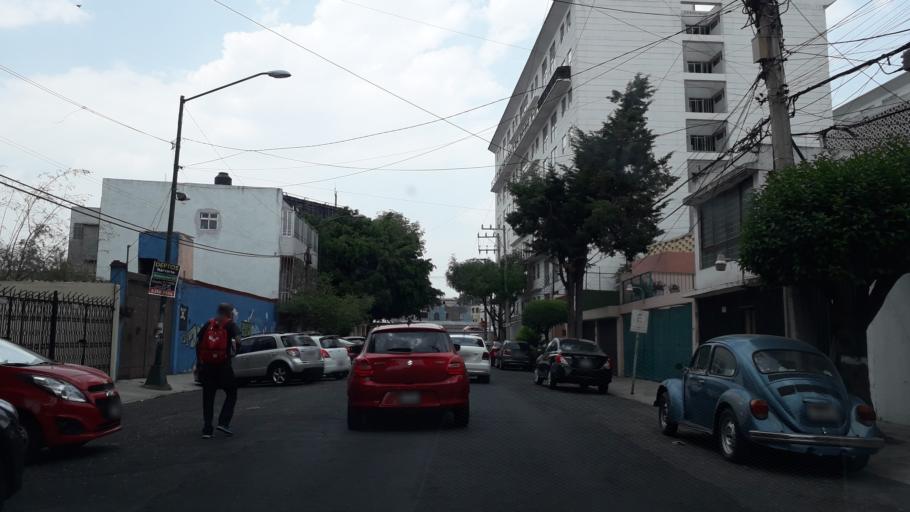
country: MX
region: Mexico City
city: Benito Juarez
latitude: 19.4029
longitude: -99.1571
